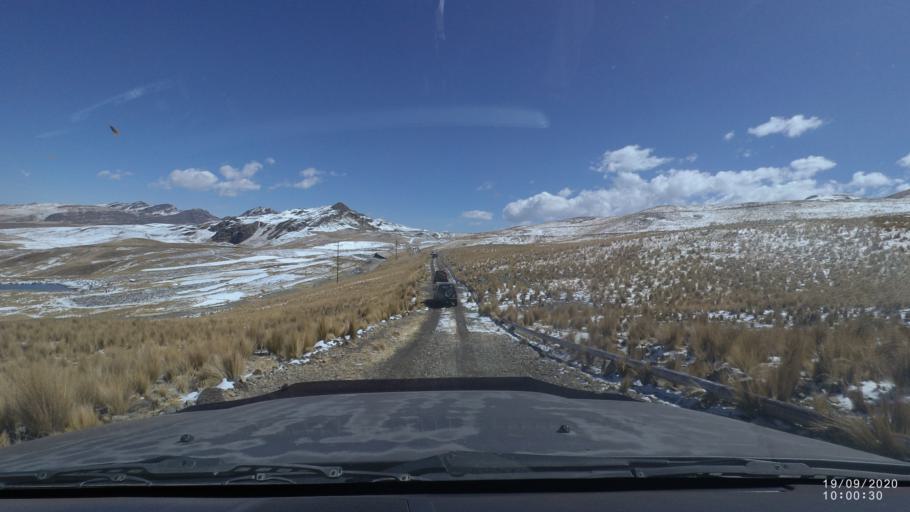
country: BO
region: Cochabamba
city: Cochabamba
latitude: -17.3046
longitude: -66.0894
